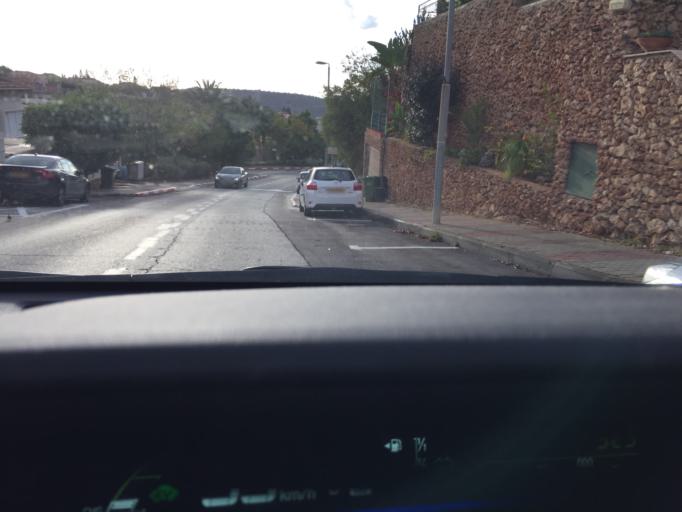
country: PS
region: West Bank
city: Az Zawiyah
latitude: 32.1078
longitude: 35.0382
